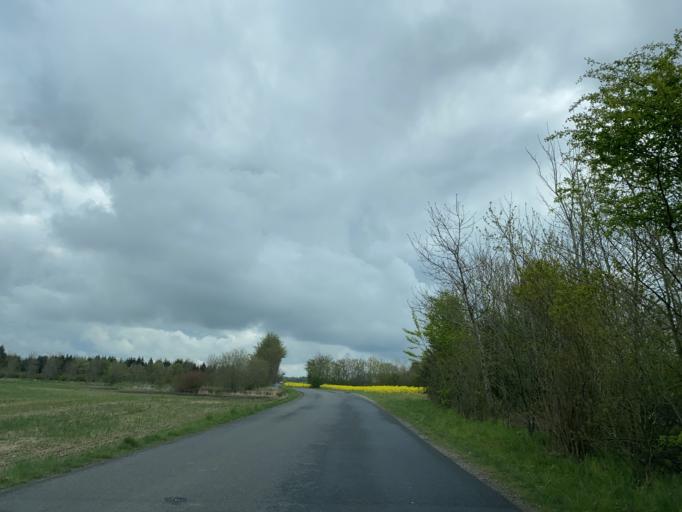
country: DK
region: Central Jutland
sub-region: Silkeborg Kommune
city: Silkeborg
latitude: 56.2249
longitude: 9.5858
